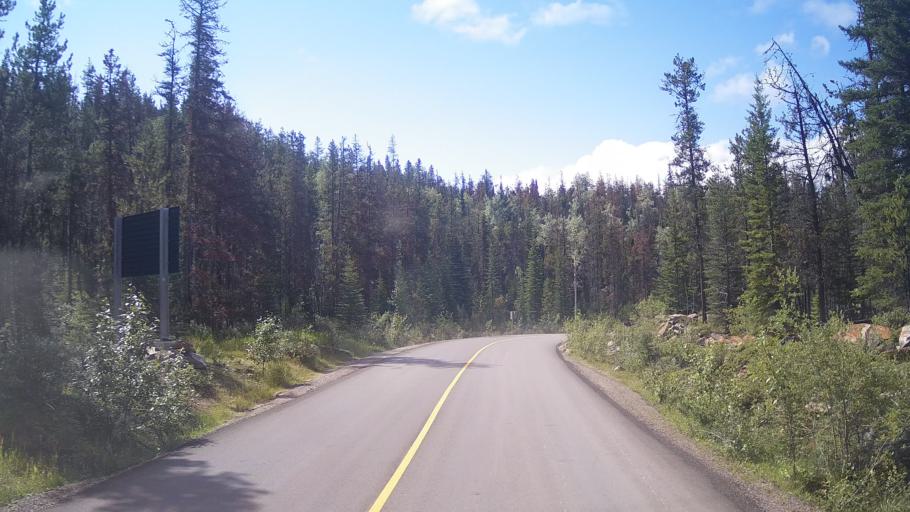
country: CA
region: Alberta
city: Jasper Park Lodge
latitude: 52.6641
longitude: -117.8848
